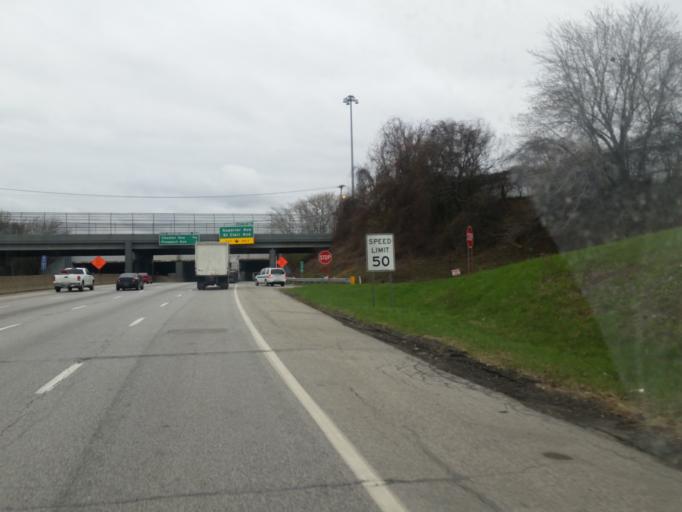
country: US
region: Ohio
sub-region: Cuyahoga County
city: Cleveland
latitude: 41.5155
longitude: -81.6746
